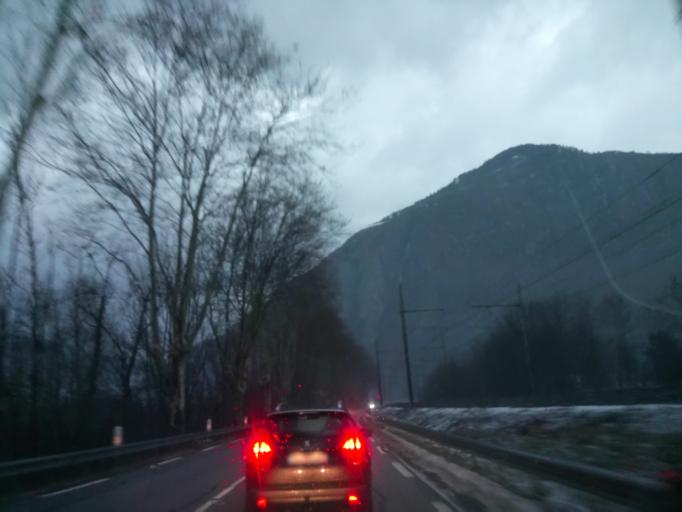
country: FR
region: Rhone-Alpes
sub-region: Departement de la Savoie
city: Saint-Etienne-de-Cuines
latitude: 45.3638
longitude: 6.2874
